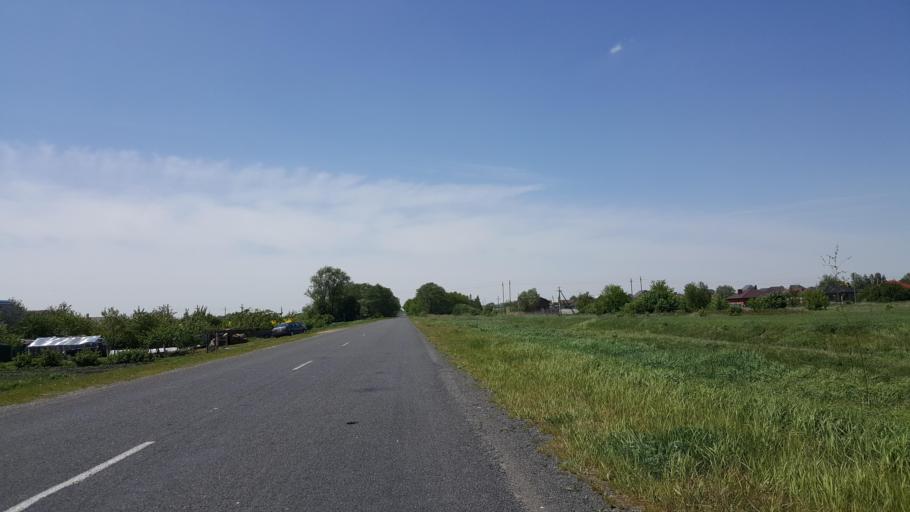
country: BY
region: Brest
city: Charnawchytsy
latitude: 52.2049
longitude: 23.7551
